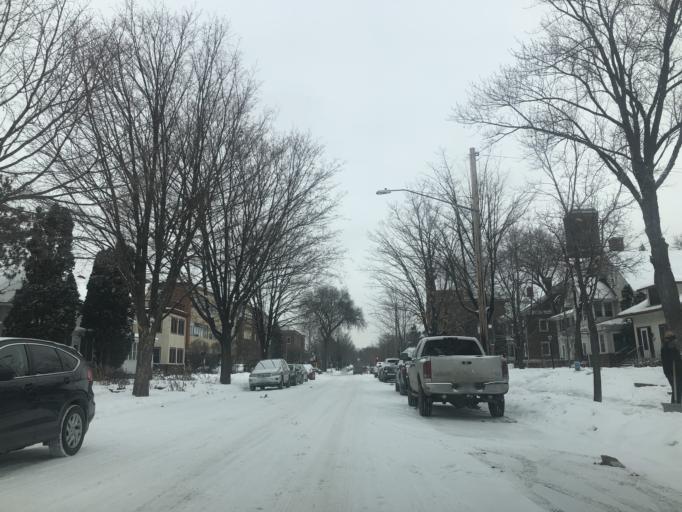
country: US
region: Minnesota
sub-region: Hennepin County
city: Richfield
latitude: 44.9327
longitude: -93.2831
